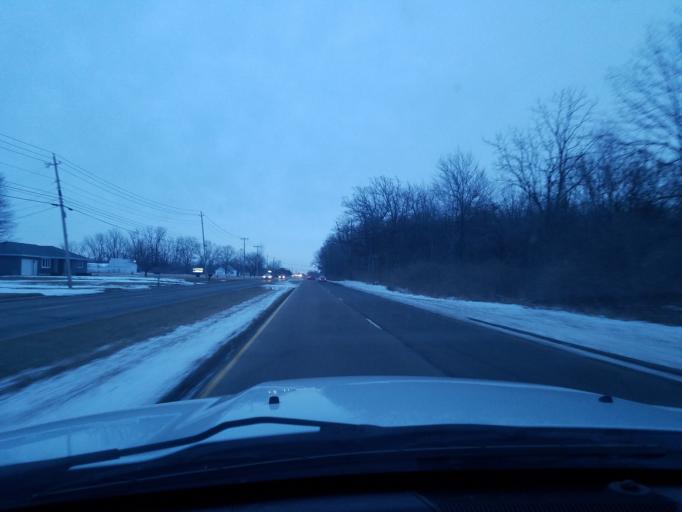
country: US
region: Indiana
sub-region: Delaware County
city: Muncie
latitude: 40.2191
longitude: -85.3529
